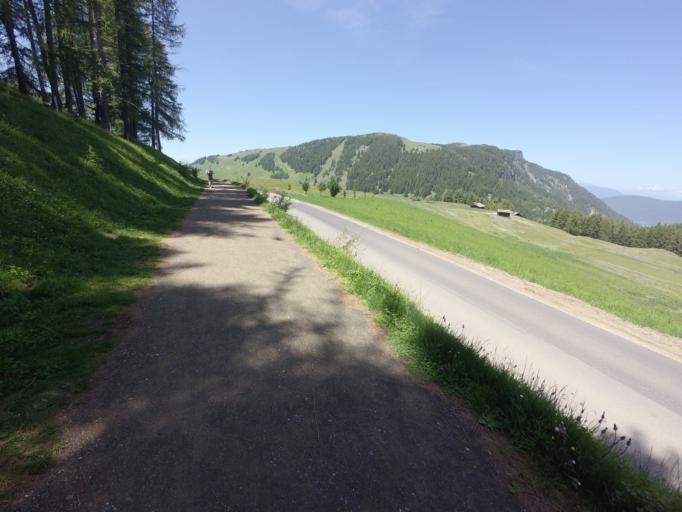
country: IT
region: Trentino-Alto Adige
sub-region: Bolzano
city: Ortisei
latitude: 46.5418
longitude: 11.6342
